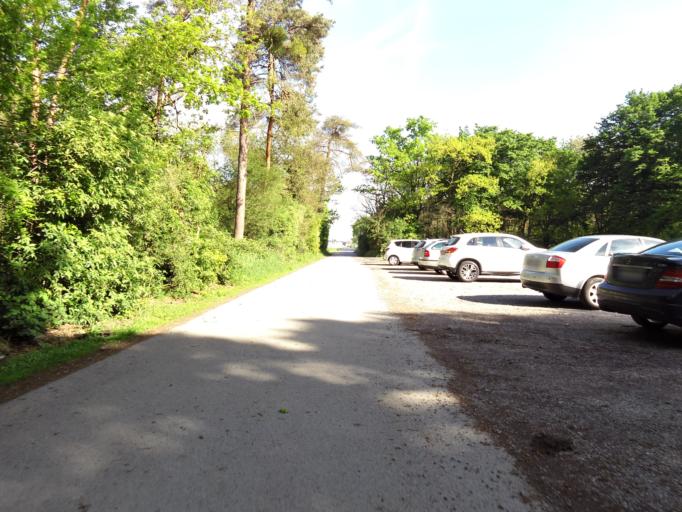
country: DE
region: Hesse
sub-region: Regierungsbezirk Darmstadt
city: Burstadt
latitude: 49.6325
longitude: 8.4833
